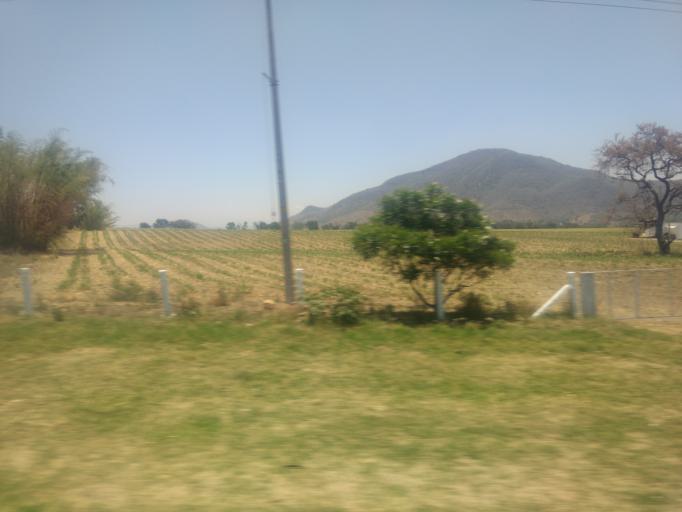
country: MX
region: Jalisco
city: Tuxpan
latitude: 19.5566
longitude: -103.4393
